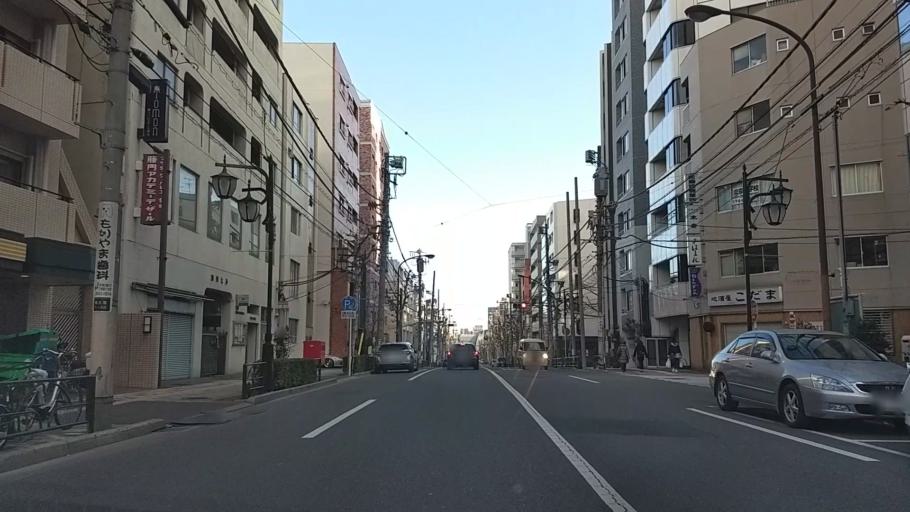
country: JP
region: Tokyo
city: Tokyo
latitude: 35.7291
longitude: 139.7315
